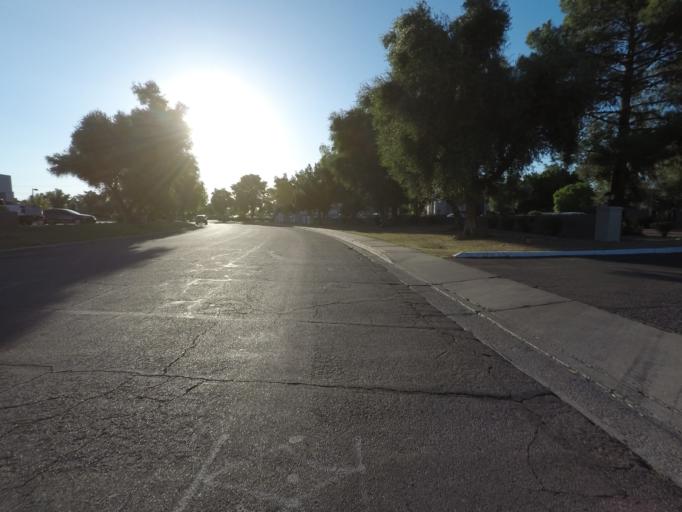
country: US
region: Arizona
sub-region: Maricopa County
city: Guadalupe
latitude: 33.3833
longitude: -111.9406
